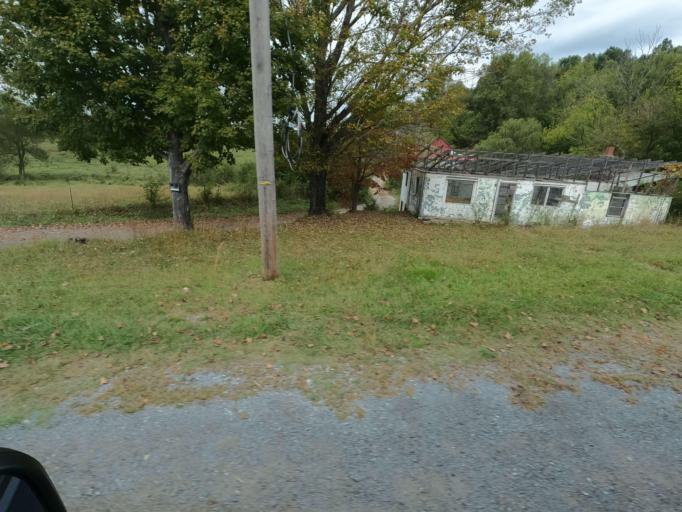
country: US
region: Tennessee
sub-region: Washington County
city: Jonesborough
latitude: 36.2217
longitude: -82.5737
